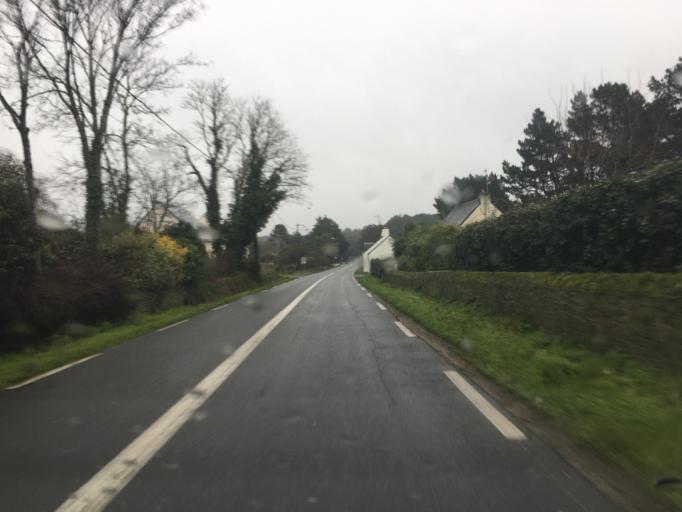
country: FR
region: Pays de la Loire
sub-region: Departement de la Loire-Atlantique
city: Guerande
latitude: 47.3351
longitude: -2.4632
